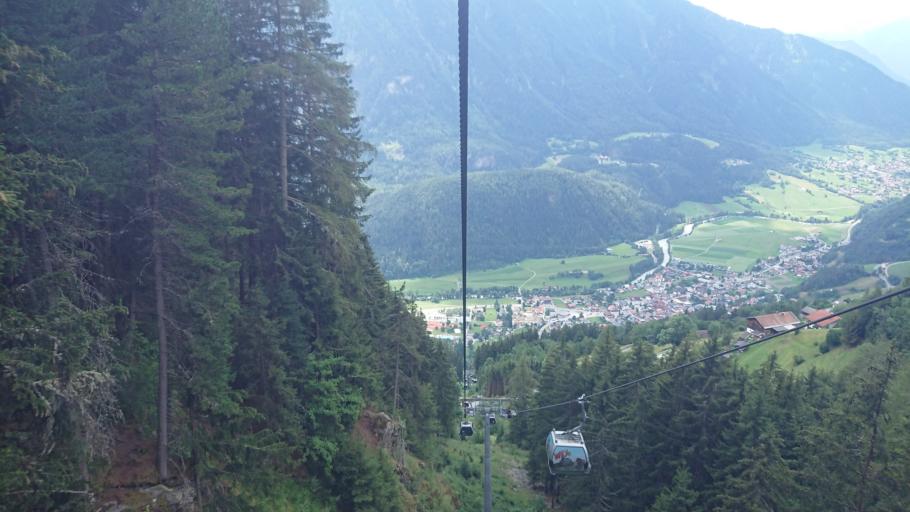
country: AT
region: Tyrol
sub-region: Politischer Bezirk Imst
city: Oetz
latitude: 47.2067
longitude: 10.9194
